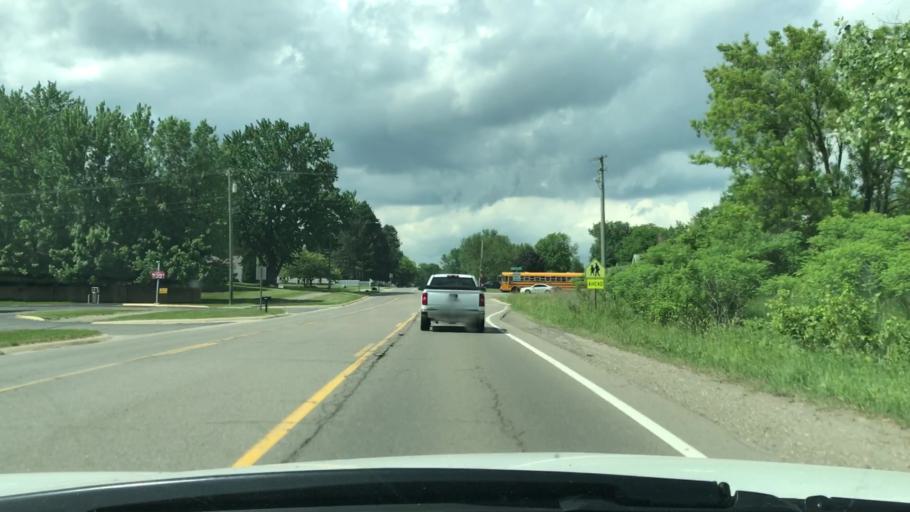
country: US
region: Michigan
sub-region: Oakland County
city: Auburn Hills
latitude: 42.7237
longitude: -83.2861
